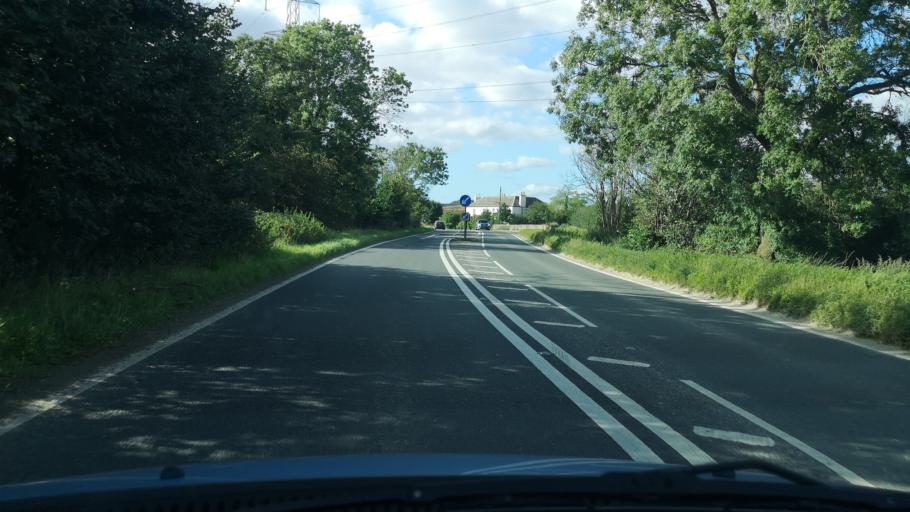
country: GB
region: England
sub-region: Doncaster
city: Marr
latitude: 53.5849
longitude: -1.2357
